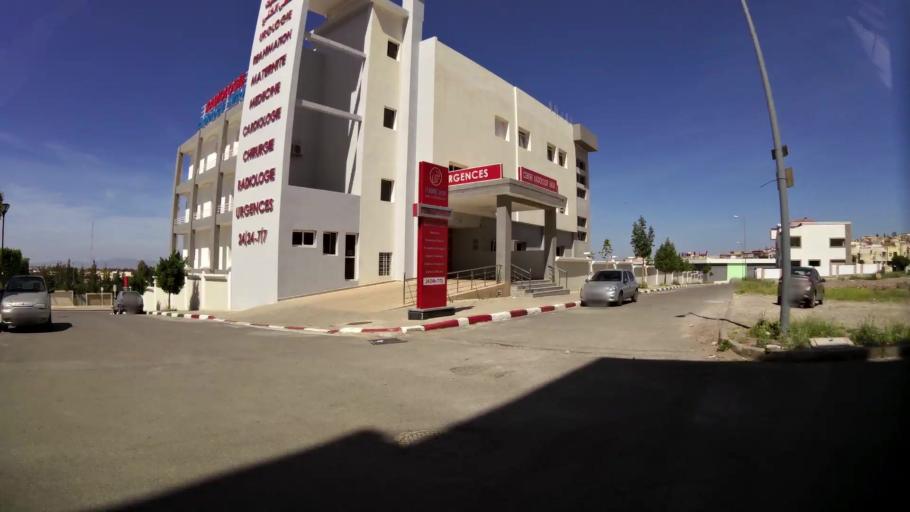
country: MA
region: Oriental
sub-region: Oujda-Angad
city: Oujda
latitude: 34.6545
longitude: -1.9094
